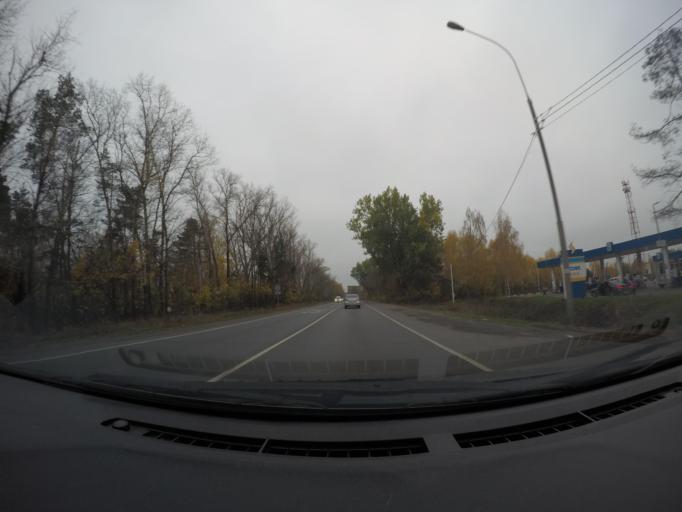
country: RU
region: Moskovskaya
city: Malyshevo
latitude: 55.4722
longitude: 38.3416
